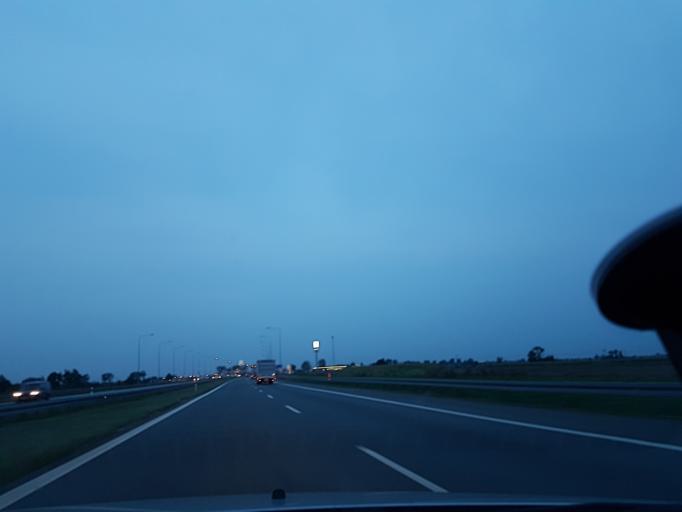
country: PL
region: Lodz Voivodeship
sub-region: Powiat kutnowski
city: Krzyzanow
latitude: 52.1918
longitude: 19.4875
